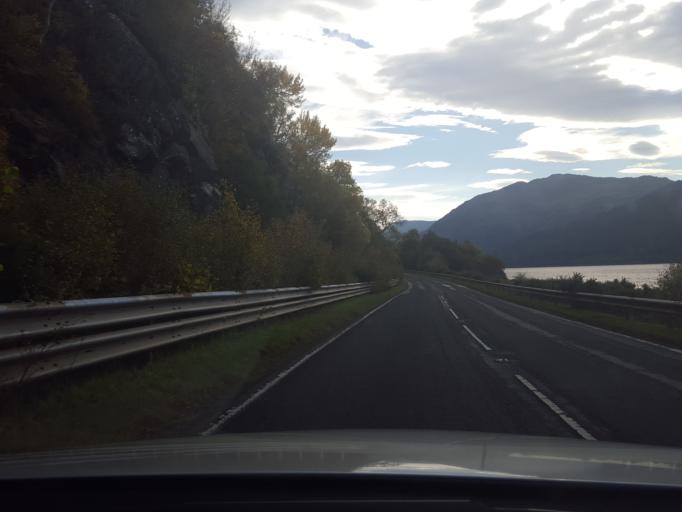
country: GB
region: Scotland
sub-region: Highland
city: Fort William
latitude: 57.2529
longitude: -5.4754
